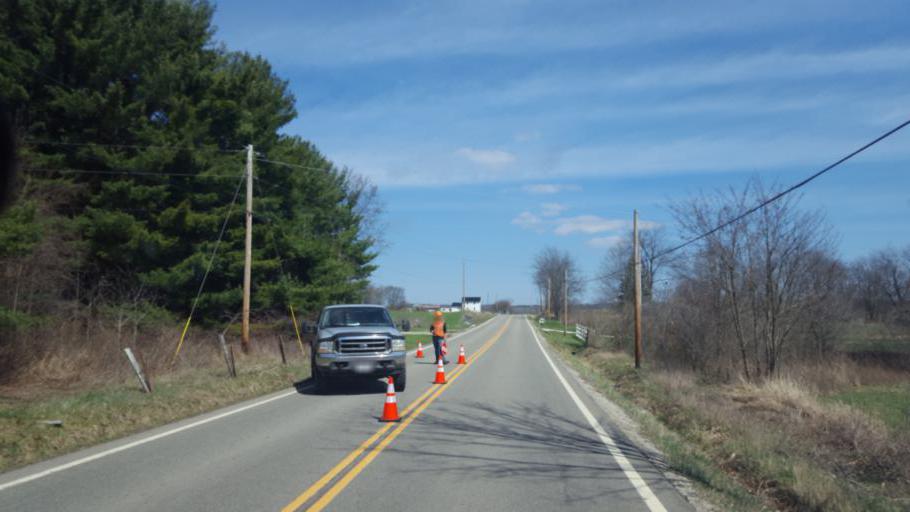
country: US
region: Ohio
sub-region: Richland County
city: Lincoln Heights
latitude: 40.8585
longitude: -82.4458
